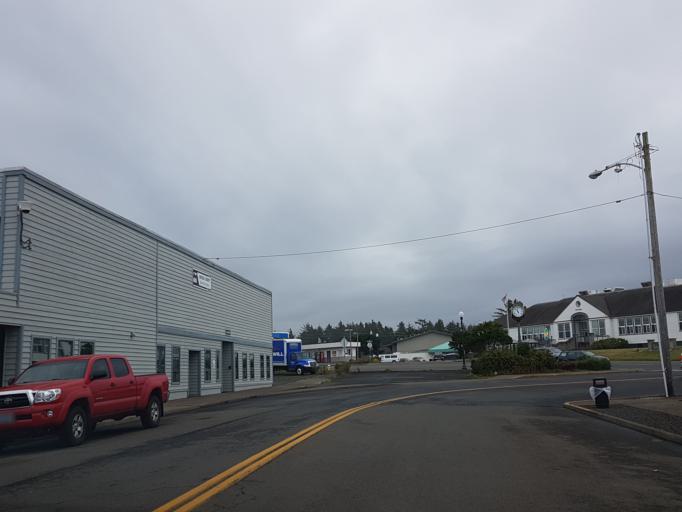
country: US
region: Oregon
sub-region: Lincoln County
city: Newport
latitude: 44.6347
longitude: -124.0551
